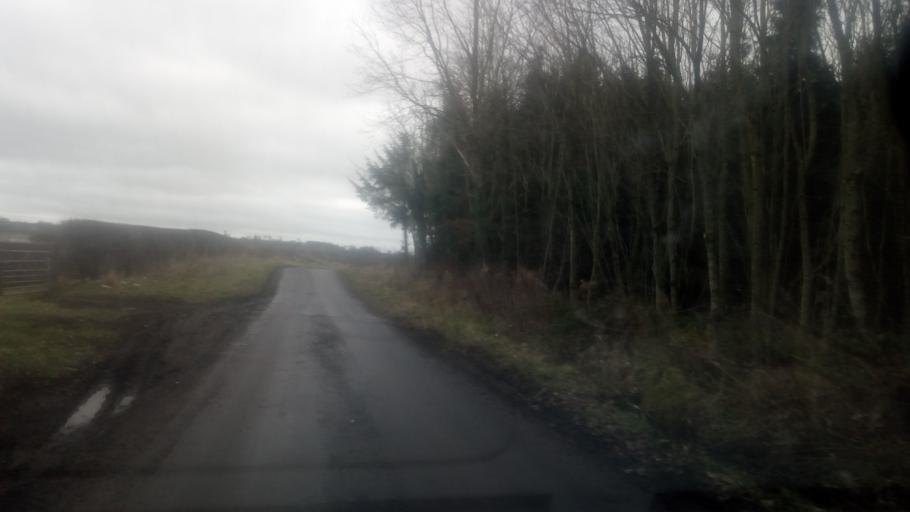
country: GB
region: Scotland
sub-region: The Scottish Borders
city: Kelso
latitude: 55.5653
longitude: -2.4821
